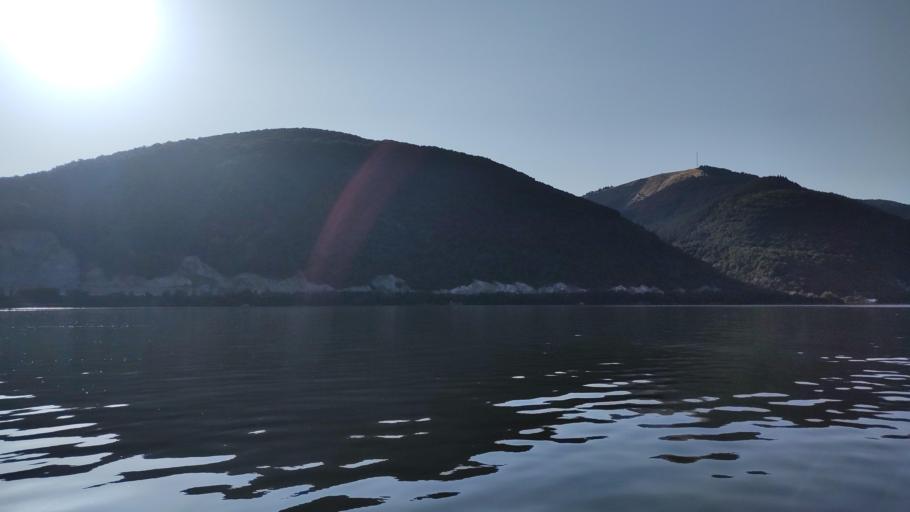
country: RO
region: Mehedinti
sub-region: Comuna Dubova
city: Dubova
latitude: 44.5451
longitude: 22.2226
